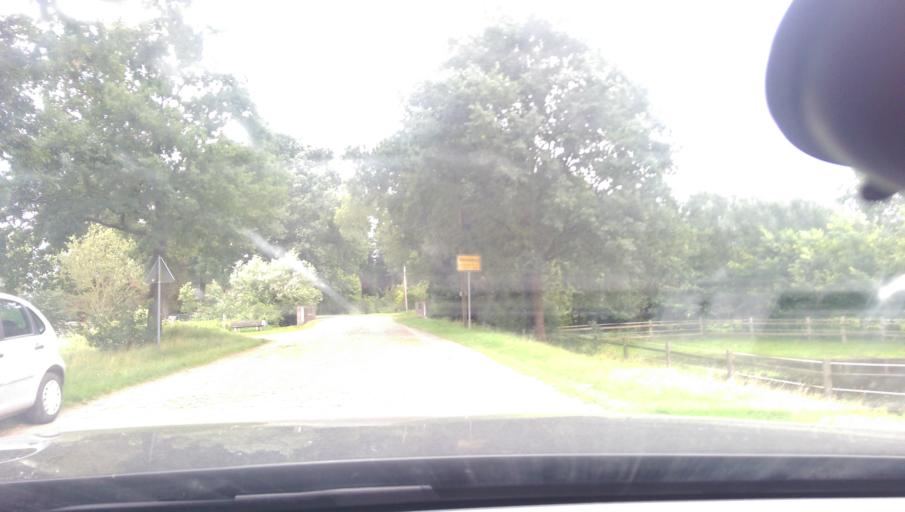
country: DE
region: Lower Saxony
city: Wietze
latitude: 52.6326
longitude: 9.8382
